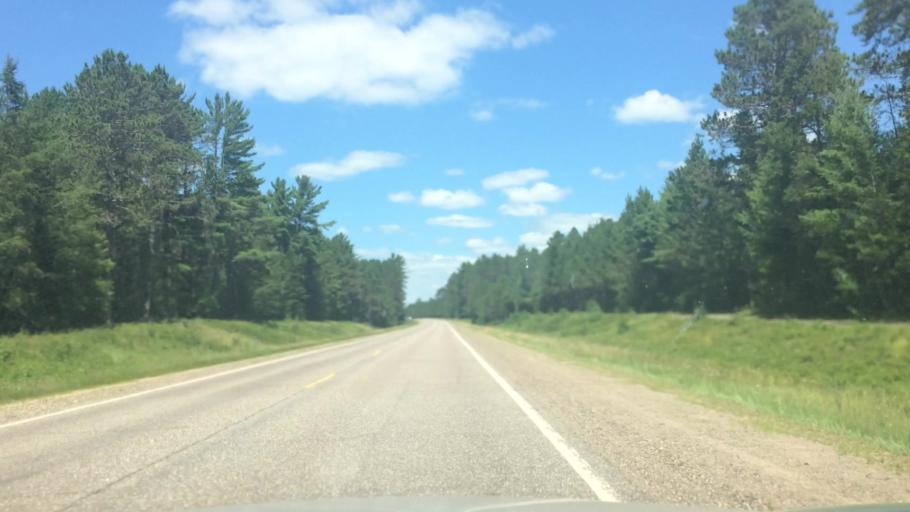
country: US
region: Wisconsin
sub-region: Vilas County
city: Lac du Flambeau
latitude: 46.0870
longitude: -89.6453
